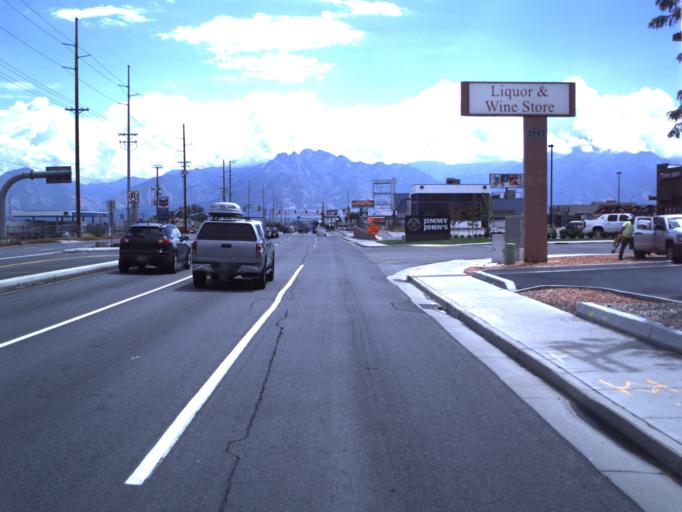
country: US
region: Utah
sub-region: Salt Lake County
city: Kearns
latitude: 40.6529
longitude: -111.9847
